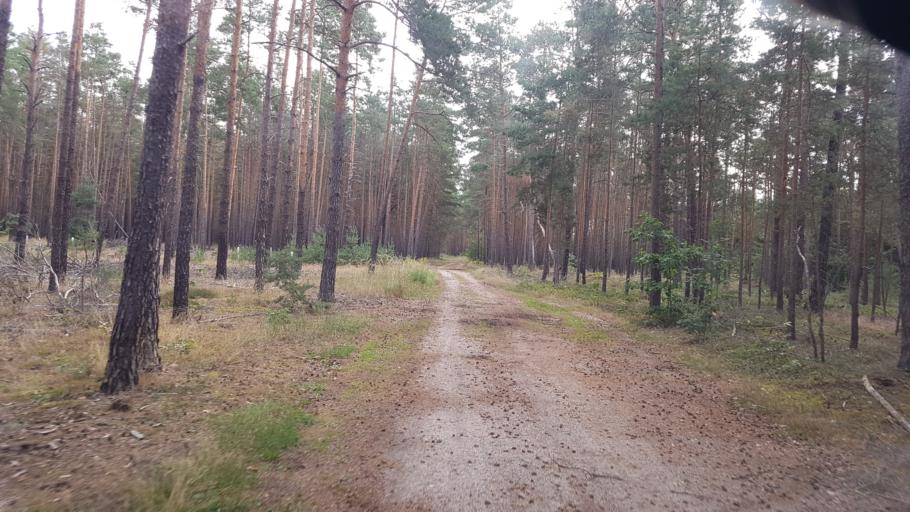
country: DE
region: Brandenburg
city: Ruckersdorf
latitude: 51.5766
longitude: 13.5917
